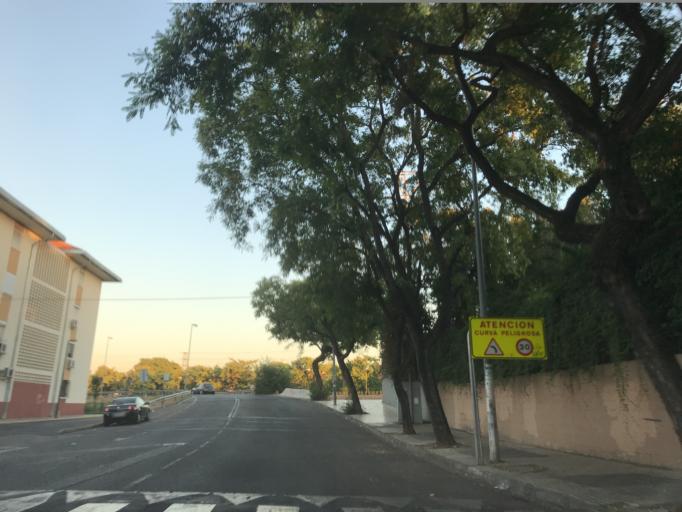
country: ES
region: Andalusia
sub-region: Provincia de Sevilla
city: Sevilla
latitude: 37.4058
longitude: -5.9258
